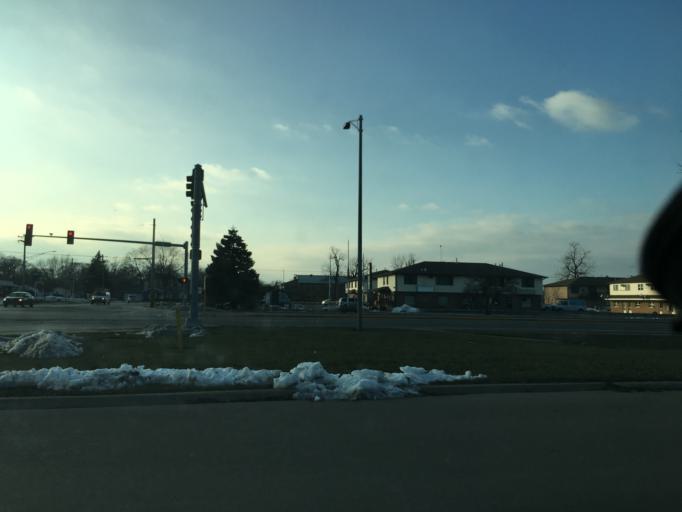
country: US
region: Illinois
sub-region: Kane County
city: Sugar Grove
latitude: 41.7619
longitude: -88.4418
